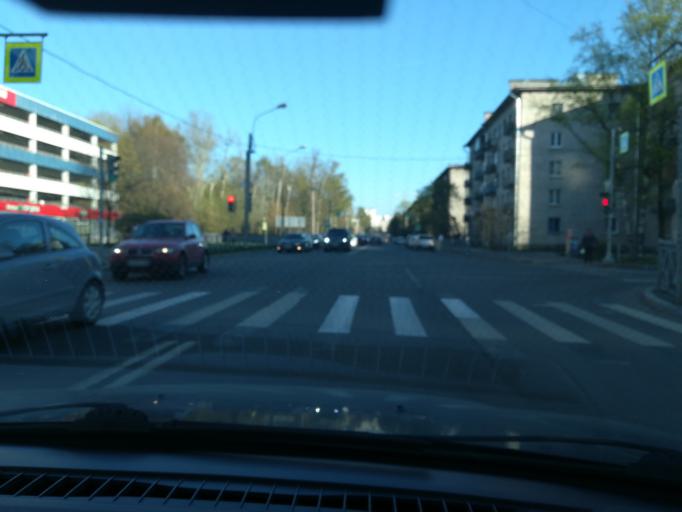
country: RU
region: St.-Petersburg
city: Vasyl'evsky Ostrov
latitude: 59.9446
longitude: 30.2375
